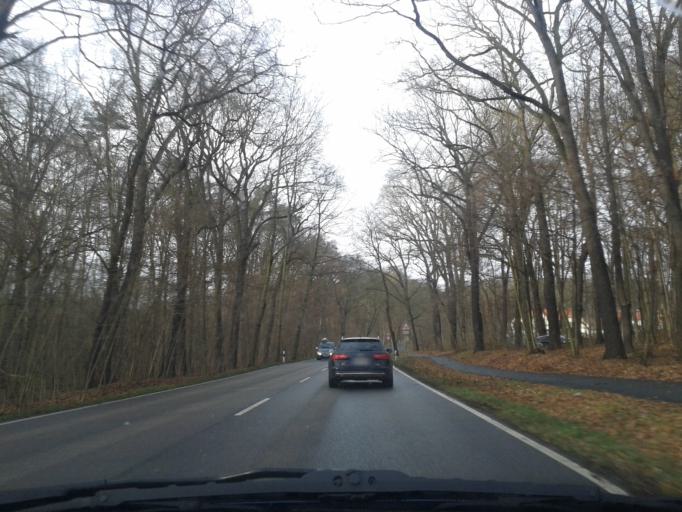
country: DE
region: Saxony
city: Radebeul
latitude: 51.1091
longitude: 13.7042
